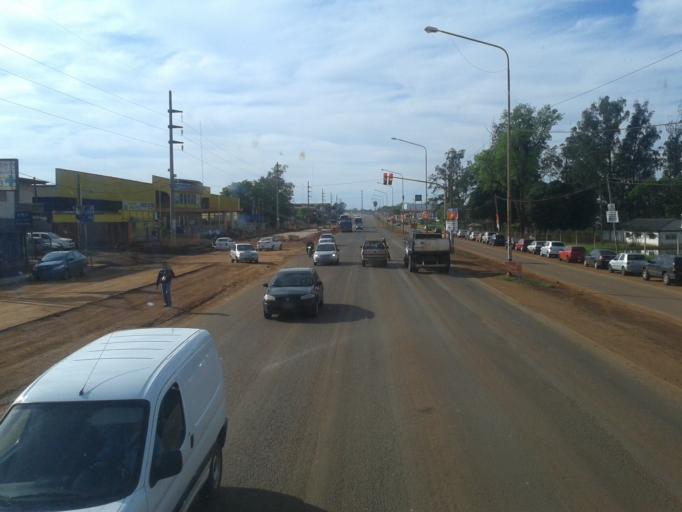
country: AR
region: Misiones
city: Garupa
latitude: -27.4462
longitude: -55.8719
